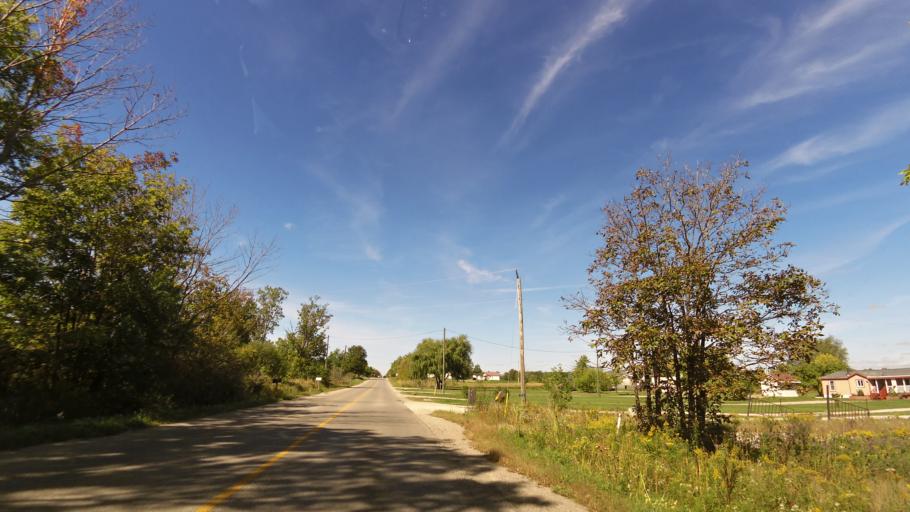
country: CA
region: Ontario
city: Brantford
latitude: 43.0734
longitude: -80.1304
